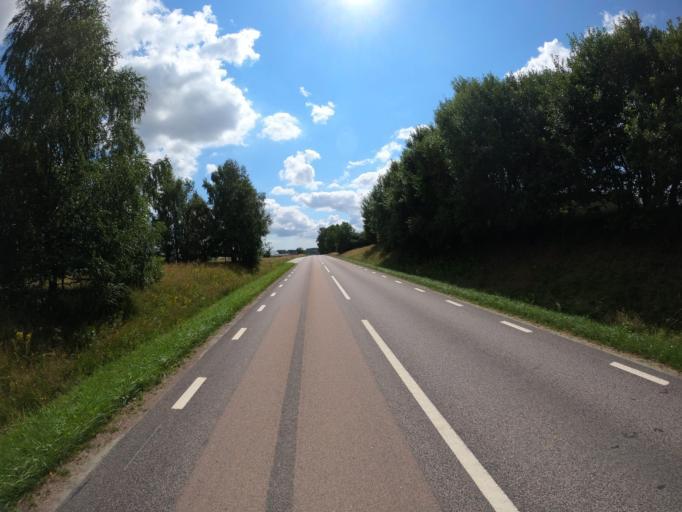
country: SE
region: Skane
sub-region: Lunds Kommun
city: Veberod
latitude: 55.6047
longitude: 13.4884
